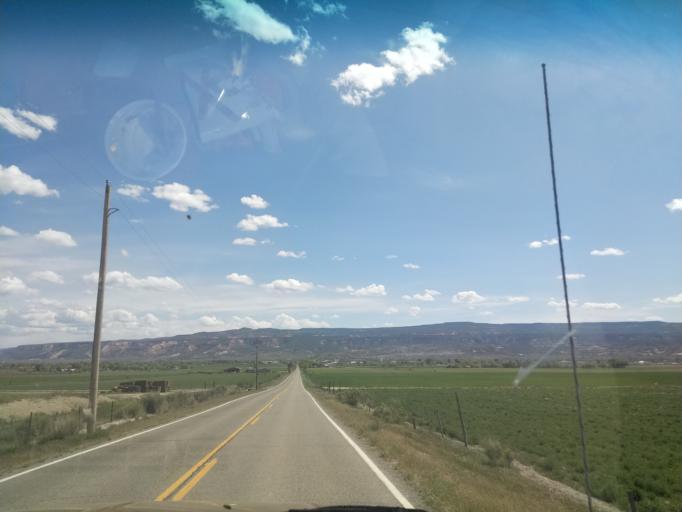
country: US
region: Colorado
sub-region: Mesa County
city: Fruita
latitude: 39.1910
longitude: -108.7571
